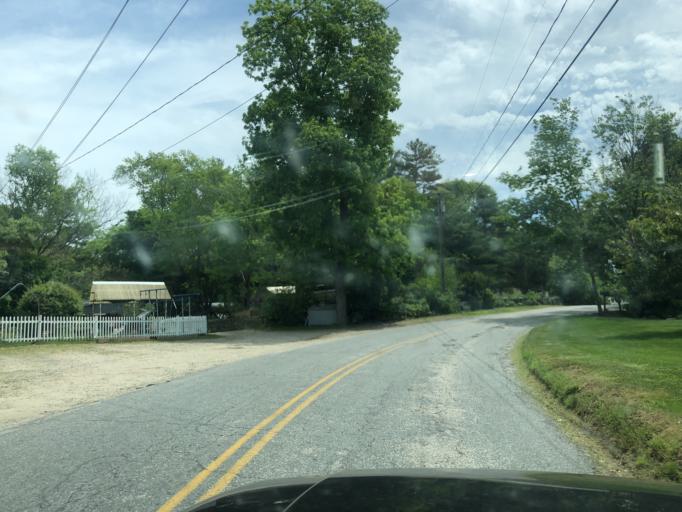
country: US
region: Connecticut
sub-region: Windham County
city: Thompson
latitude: 41.9642
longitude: -71.8246
